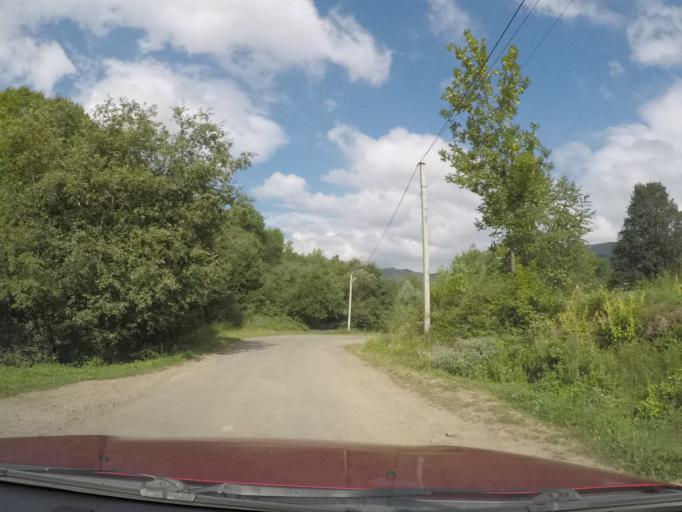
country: UA
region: Zakarpattia
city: Velykyi Bereznyi
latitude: 48.9461
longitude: 22.6792
